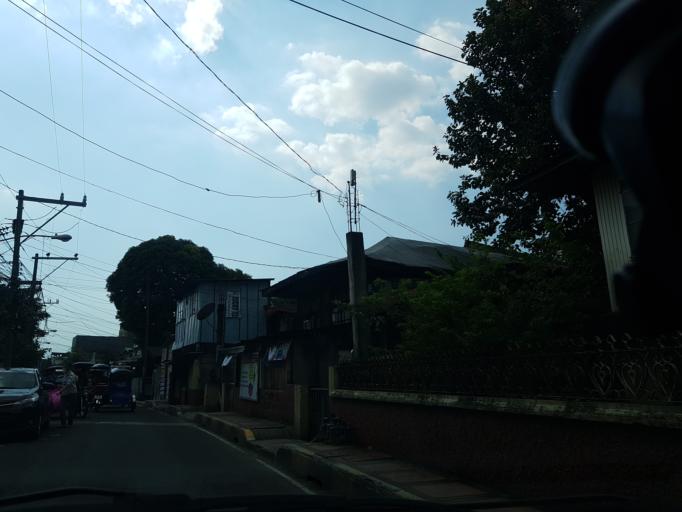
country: PH
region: Calabarzon
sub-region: Province of Rizal
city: Pateros
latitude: 14.5642
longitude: 121.0876
